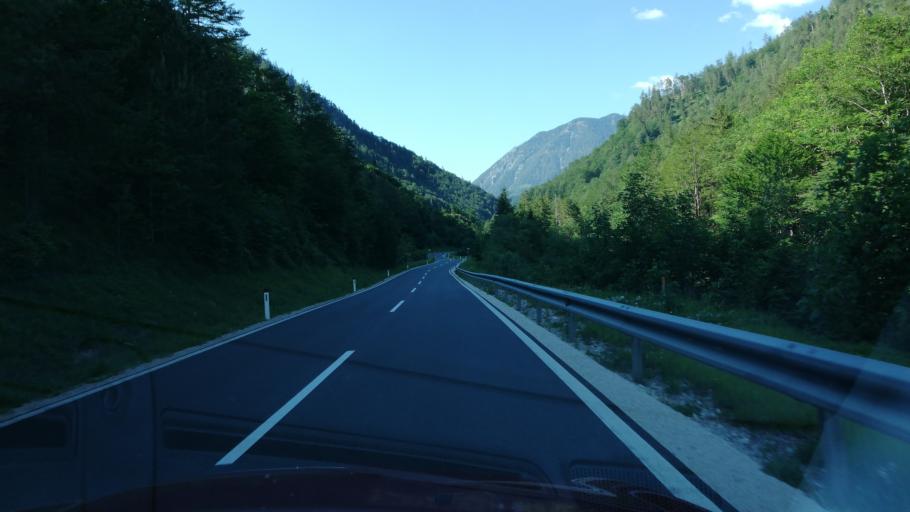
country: AT
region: Upper Austria
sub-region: Politischer Bezirk Kirchdorf an der Krems
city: Rossleithen
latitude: 47.7518
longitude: 14.1625
